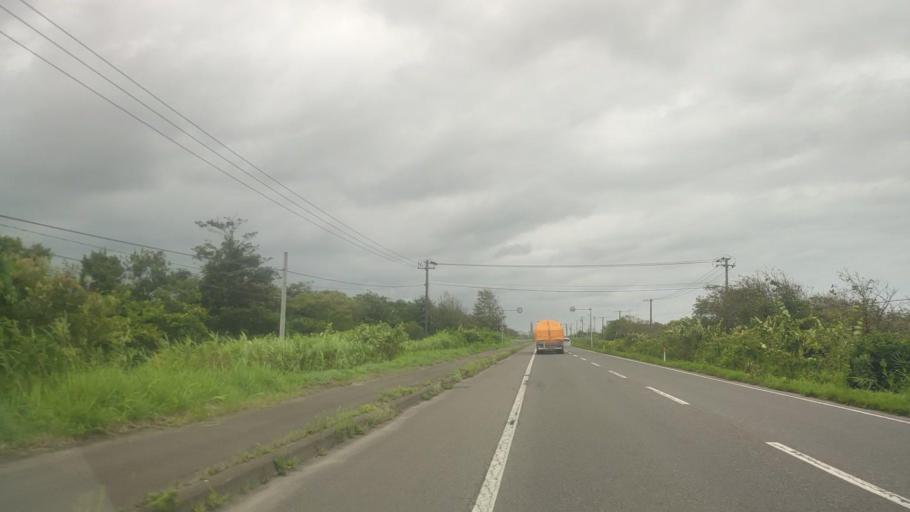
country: JP
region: Hokkaido
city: Shiraoi
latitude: 42.4963
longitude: 141.2668
